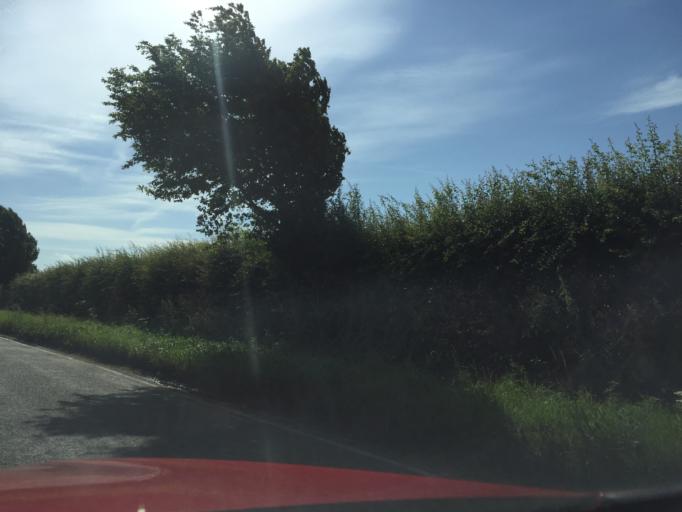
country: GB
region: England
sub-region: Gloucestershire
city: Stonehouse
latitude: 51.7962
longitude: -2.3371
